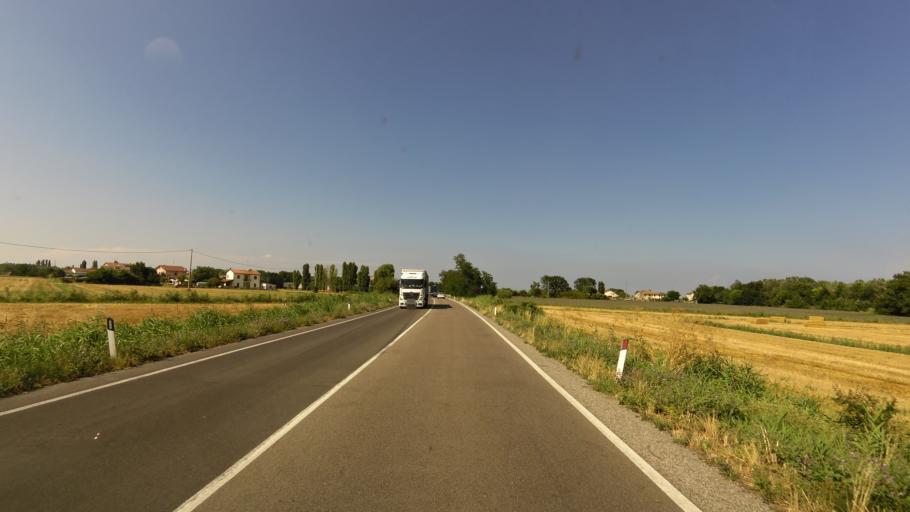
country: IT
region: Emilia-Romagna
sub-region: Provincia di Ravenna
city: Marina Romea
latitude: 44.5602
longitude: 12.2481
